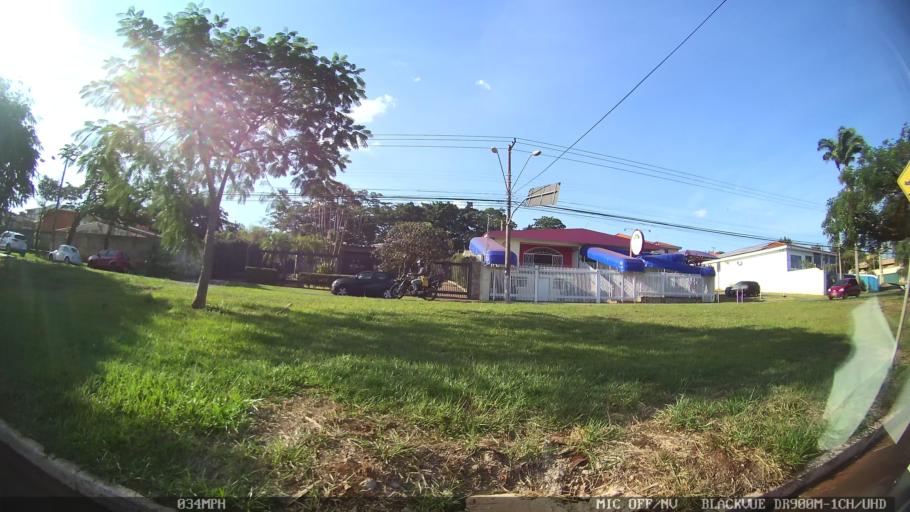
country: BR
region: Sao Paulo
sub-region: Ribeirao Preto
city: Ribeirao Preto
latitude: -21.2003
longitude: -47.7898
